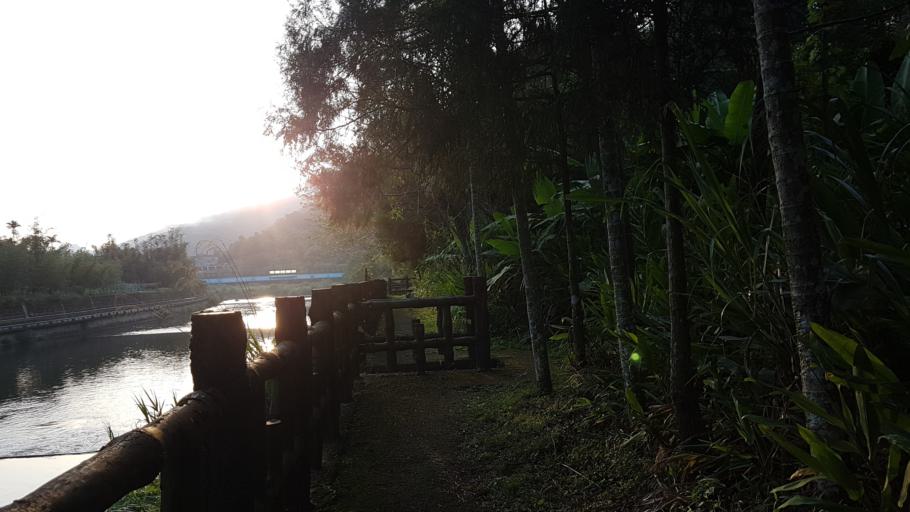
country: TW
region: Taiwan
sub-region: Yilan
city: Yilan
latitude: 24.9340
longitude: 121.7024
